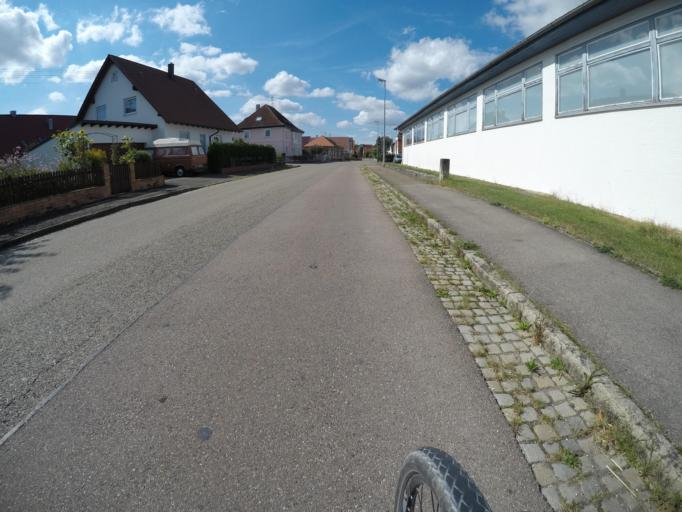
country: DE
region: Bavaria
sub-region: Swabia
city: Bachhagel
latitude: 48.6324
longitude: 10.3248
